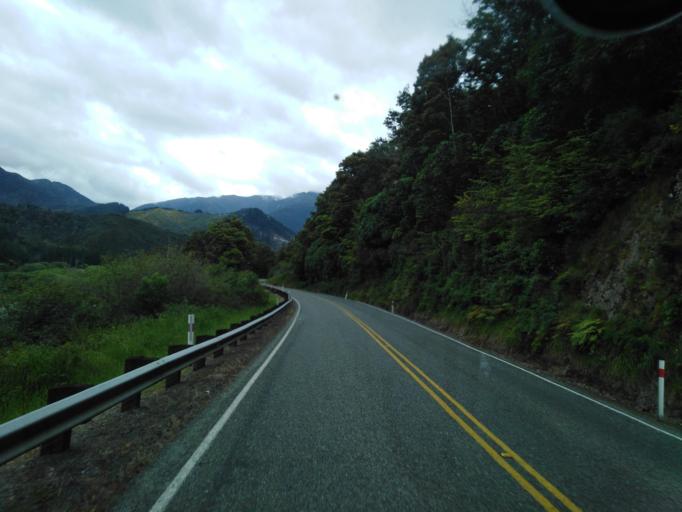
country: NZ
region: Tasman
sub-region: Tasman District
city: Wakefield
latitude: -41.7059
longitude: 172.5857
